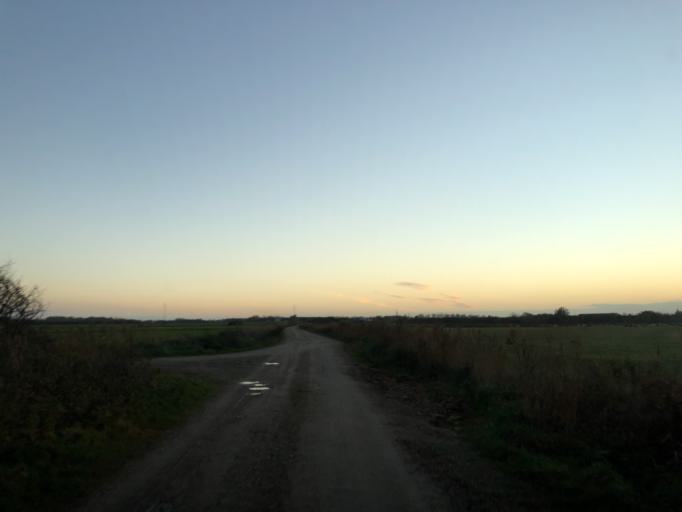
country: DK
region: Central Jutland
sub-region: Holstebro Kommune
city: Ulfborg
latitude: 56.2877
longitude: 8.2927
